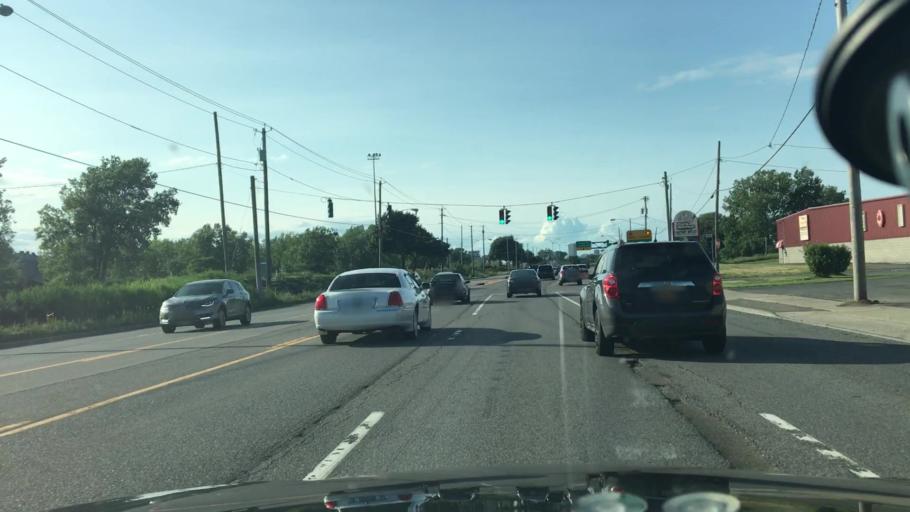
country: US
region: New York
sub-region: Erie County
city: Lackawanna
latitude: 42.8204
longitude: -78.8482
